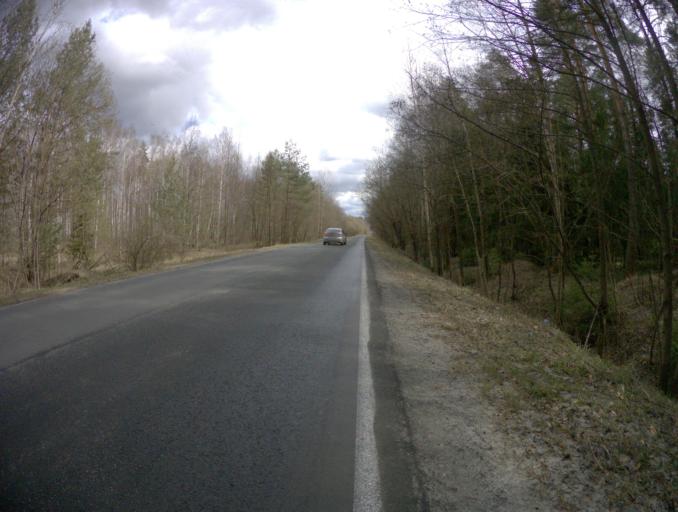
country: RU
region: Vladimir
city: Sudogda
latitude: 56.0747
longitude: 40.7736
